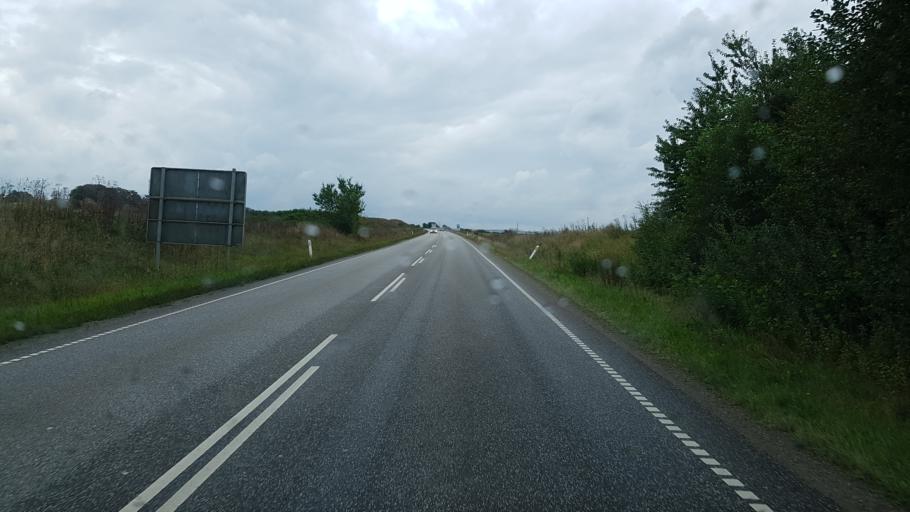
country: DK
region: Central Jutland
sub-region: Horsens Kommune
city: Horsens
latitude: 55.8957
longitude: 9.7551
